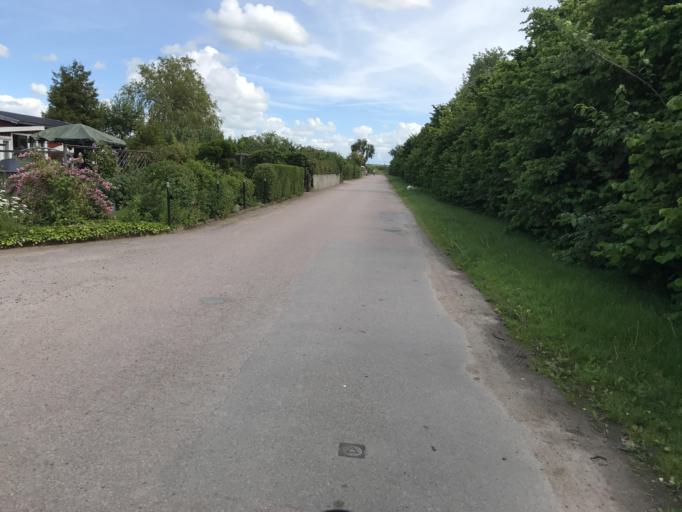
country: SE
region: Skane
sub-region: Landskrona
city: Landskrona
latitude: 55.8937
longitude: 12.8500
